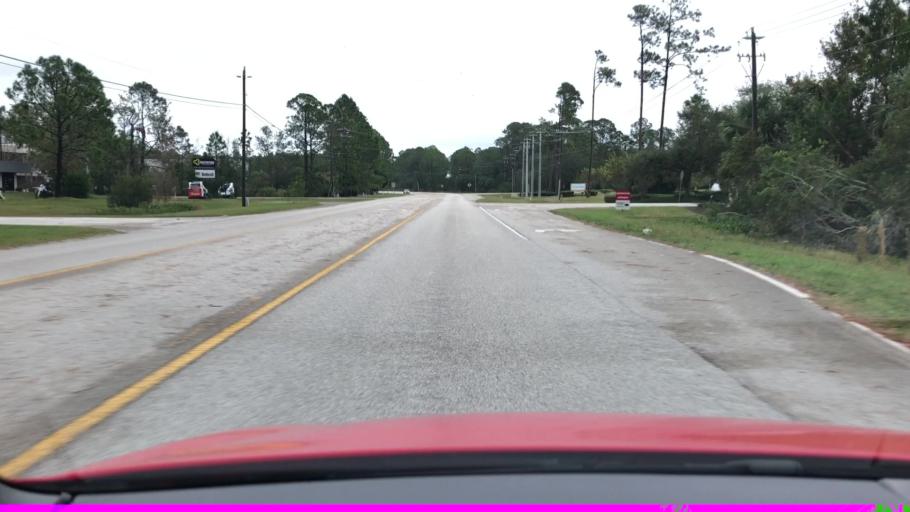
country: US
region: Florida
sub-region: Volusia County
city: Holly Hill
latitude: 29.2107
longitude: -81.0794
